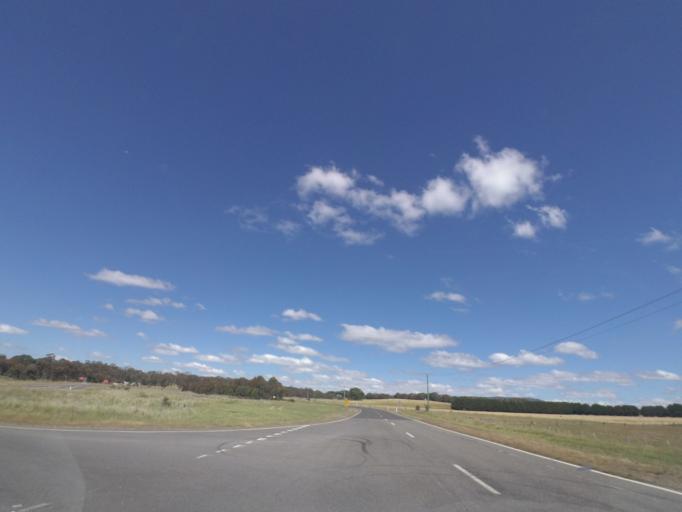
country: AU
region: Victoria
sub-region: Hume
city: Sunbury
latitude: -37.2964
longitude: 144.5000
